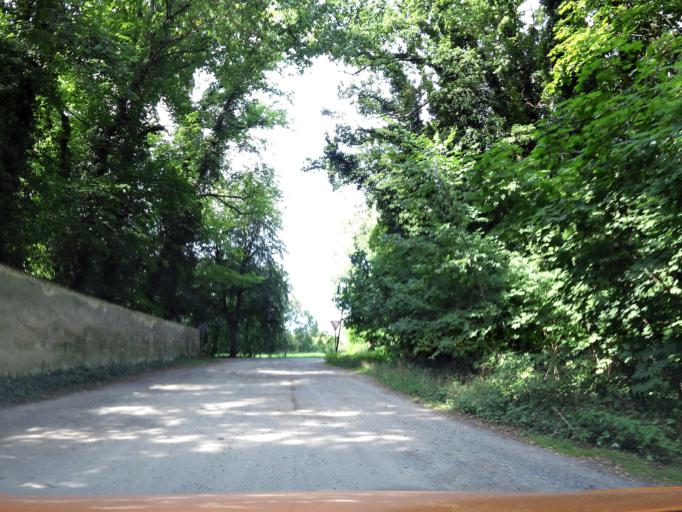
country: DE
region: Brandenburg
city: Trebbin
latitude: 52.2414
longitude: 13.1295
